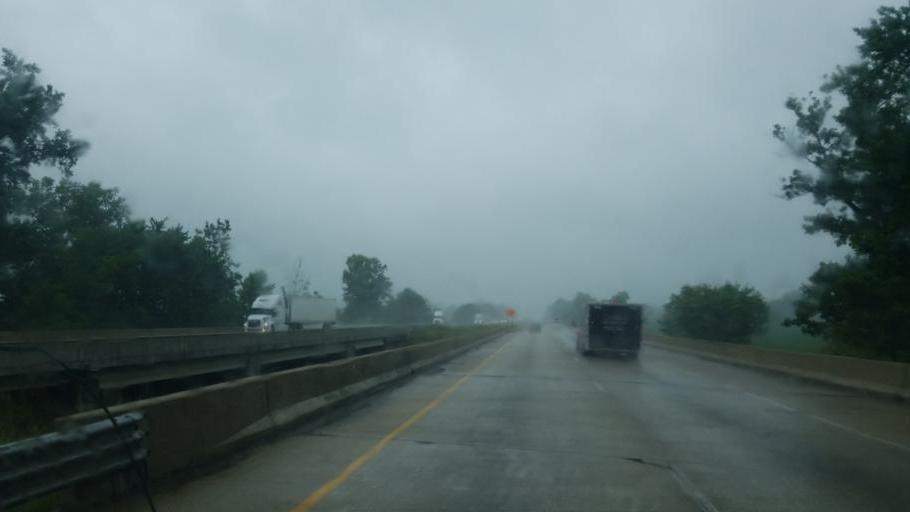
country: US
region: Indiana
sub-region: Putnam County
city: Cloverdale
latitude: 39.5613
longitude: -86.6525
